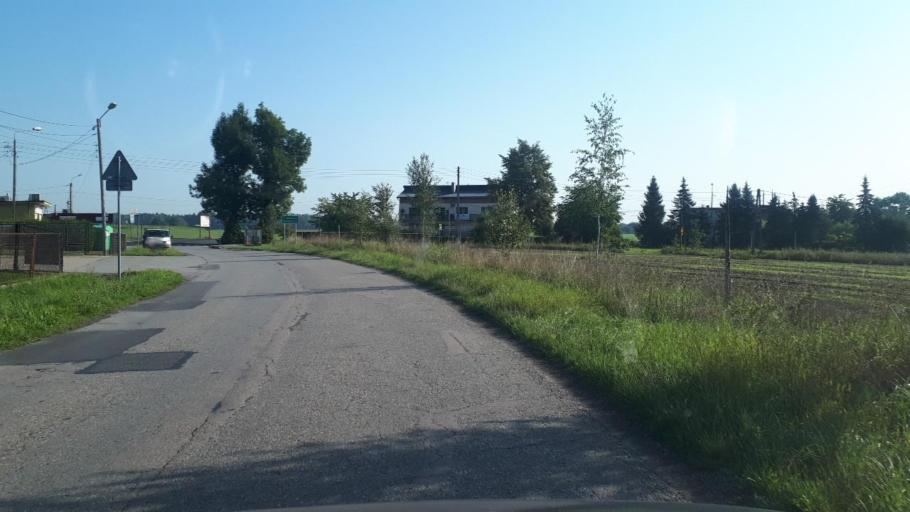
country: PL
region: Silesian Voivodeship
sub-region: Powiat bielski
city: Bronow
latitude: 49.8796
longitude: 18.8718
